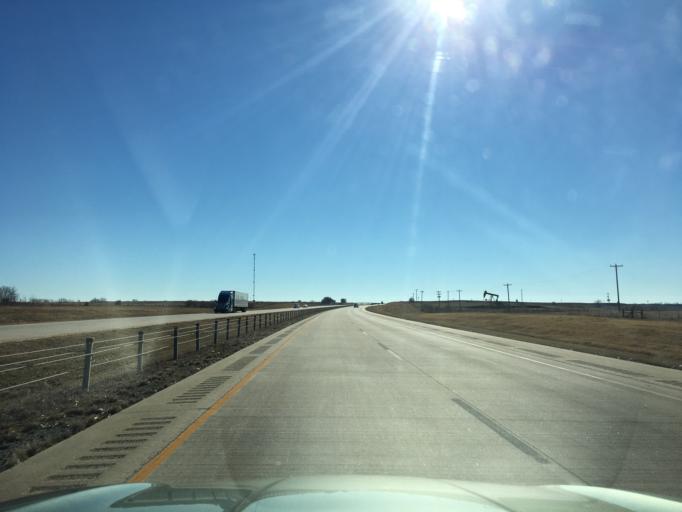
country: US
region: Oklahoma
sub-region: Kay County
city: Tonkawa
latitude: 36.5194
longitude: -97.3378
